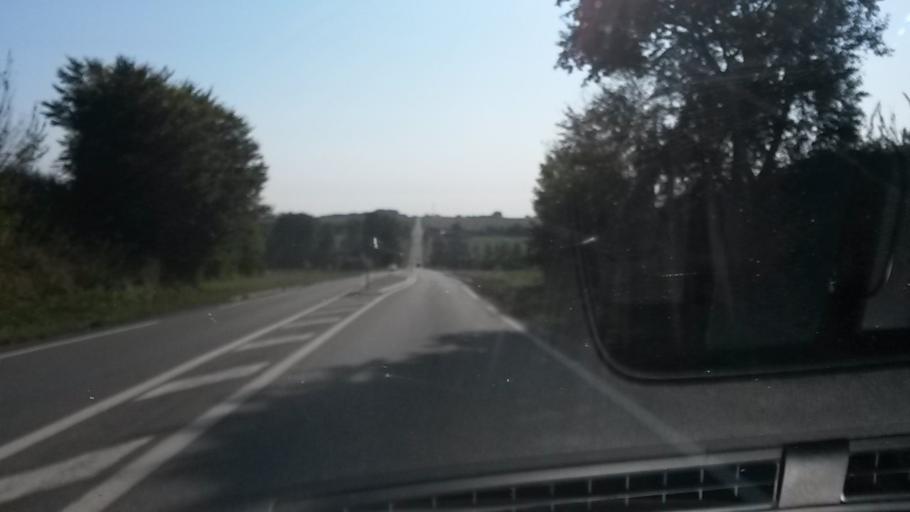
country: FR
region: Picardie
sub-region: Departement de l'Aisne
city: Ribemont
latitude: 49.8416
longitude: 3.4350
